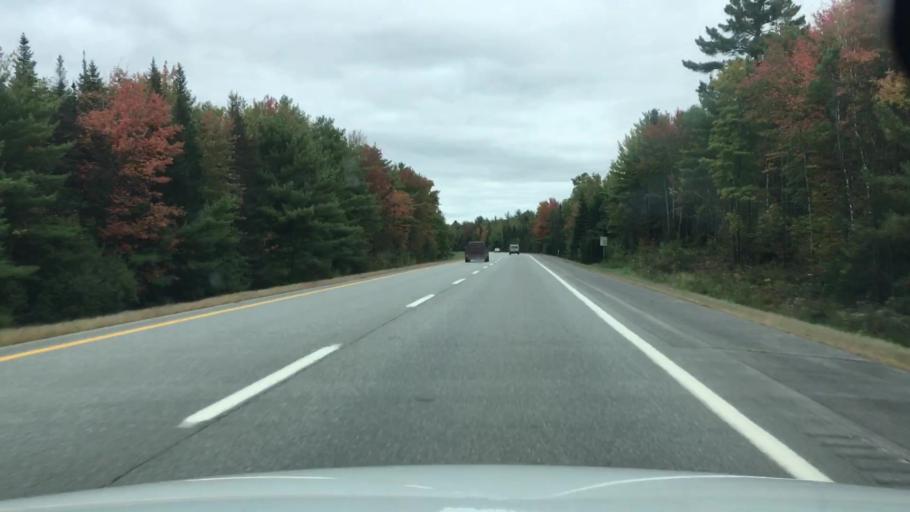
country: US
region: Maine
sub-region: Penobscot County
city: Plymouth
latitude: 44.7957
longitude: -69.2111
